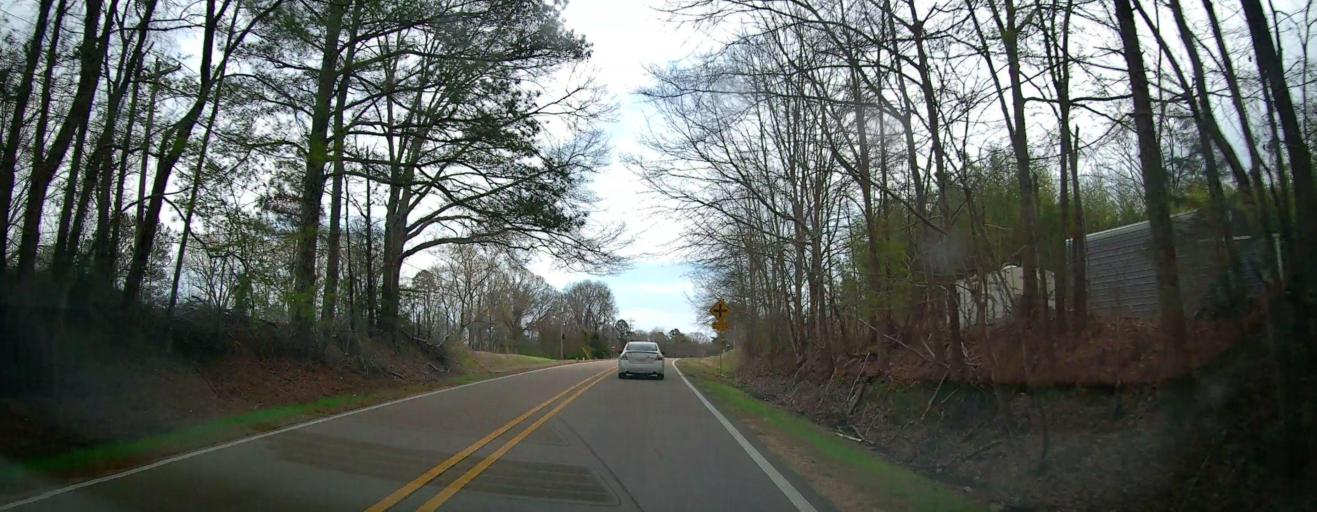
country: US
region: Mississippi
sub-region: Itawamba County
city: Fulton
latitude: 34.2740
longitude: -88.3449
